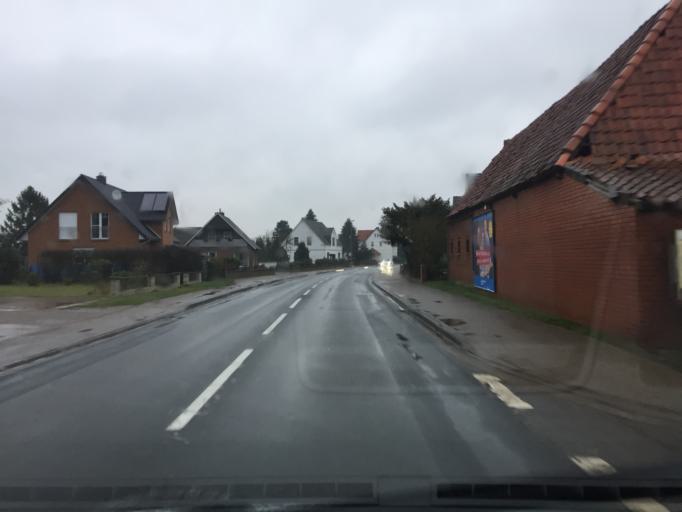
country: DE
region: Lower Saxony
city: Thedinghausen
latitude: 52.9569
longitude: 9.0149
